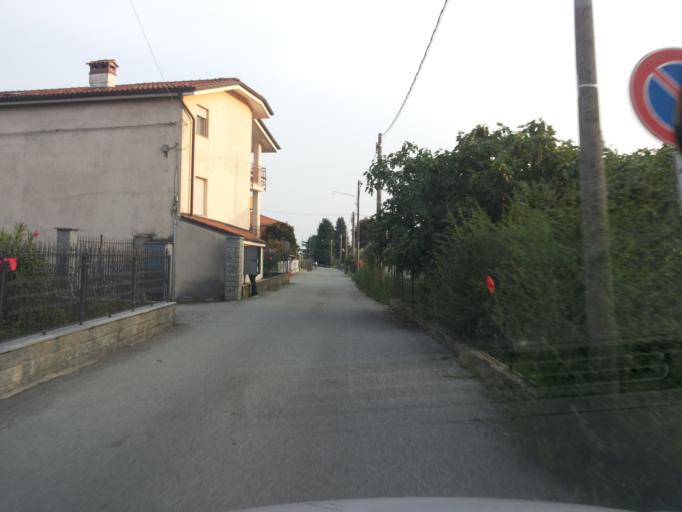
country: IT
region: Piedmont
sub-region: Provincia di Biella
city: Cavaglia
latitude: 45.4003
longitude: 8.0926
